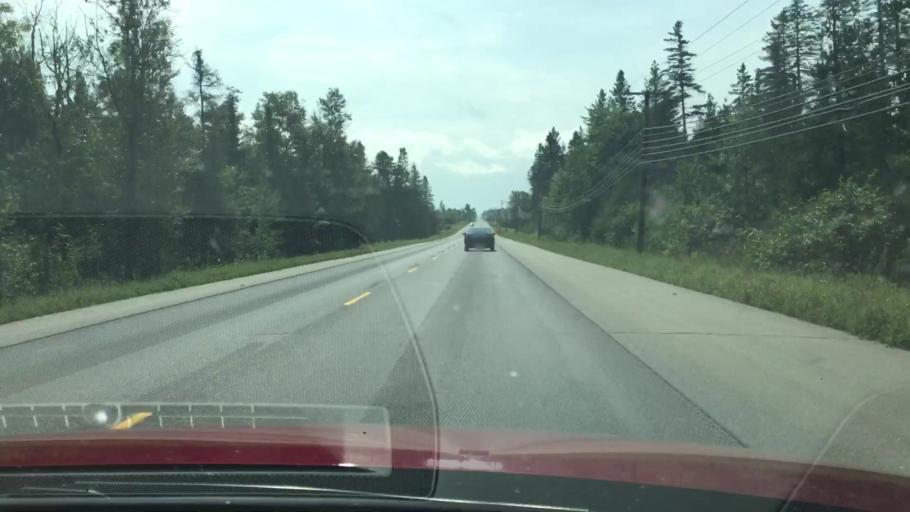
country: US
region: Maine
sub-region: Aroostook County
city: Houlton
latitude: 46.2564
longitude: -67.8407
